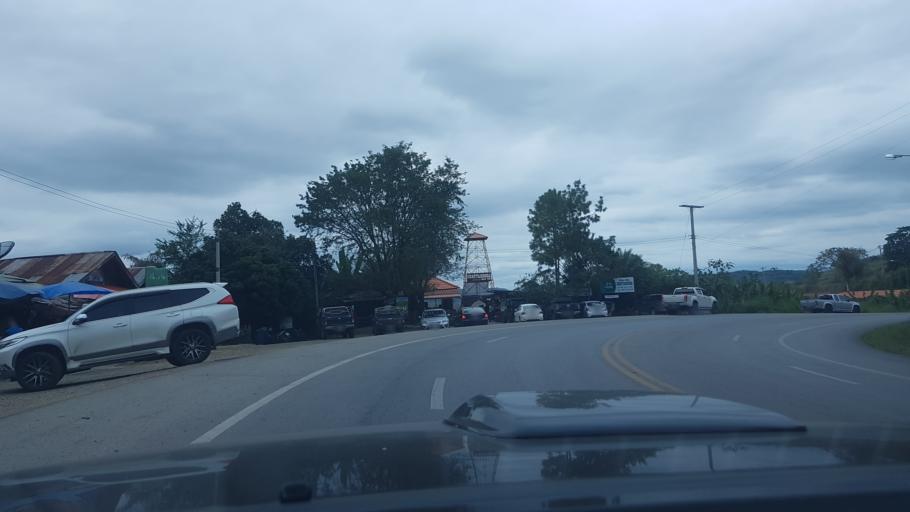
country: TH
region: Phetchabun
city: Khao Kho
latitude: 16.5572
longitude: 101.0255
